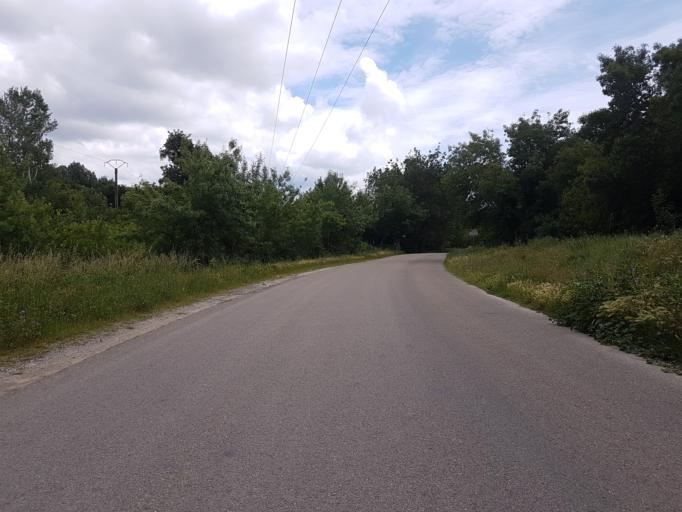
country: FR
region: Languedoc-Roussillon
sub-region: Departement du Gard
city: Beaucaire
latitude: 43.8173
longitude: 4.6397
